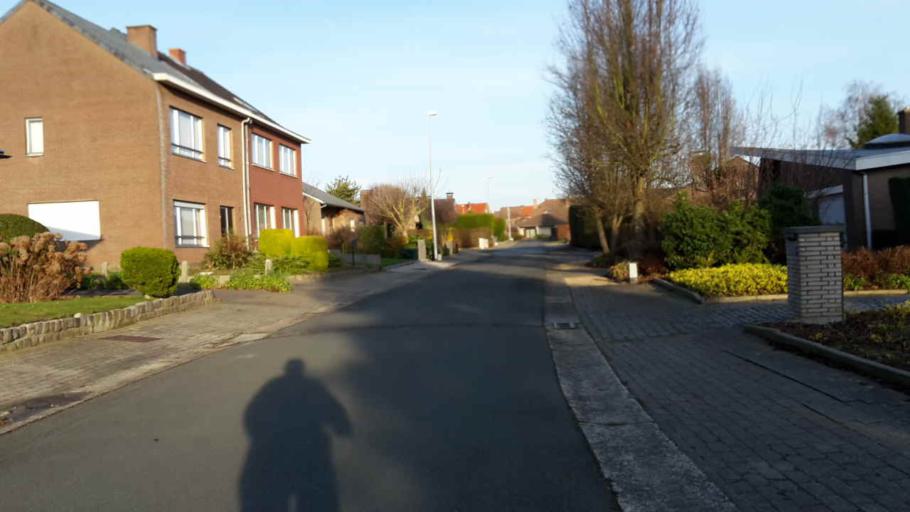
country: BE
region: Flanders
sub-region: Provincie Vlaams-Brabant
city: Hoegaarden
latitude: 50.8209
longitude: 4.8824
